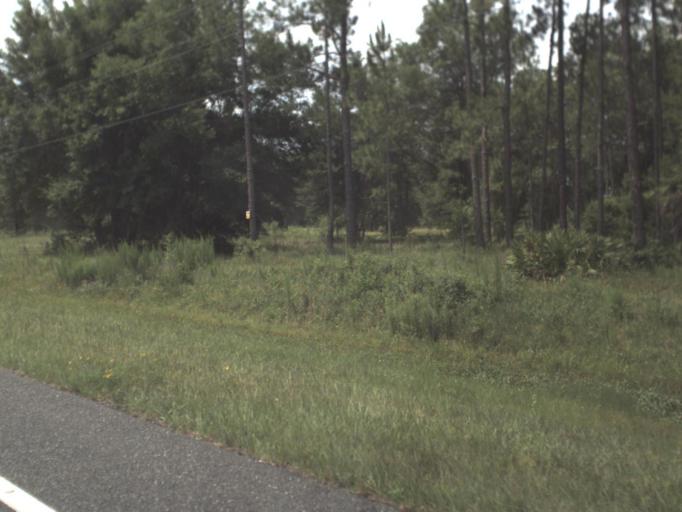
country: US
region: Florida
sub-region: Levy County
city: Chiefland
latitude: 29.4028
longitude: -82.8148
